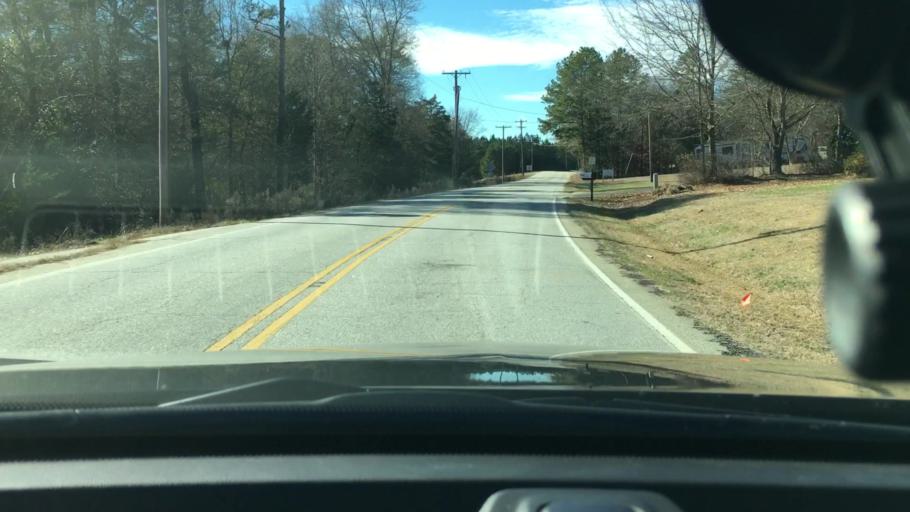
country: US
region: South Carolina
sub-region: Spartanburg County
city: Pacolet
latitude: 34.9172
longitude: -81.7526
